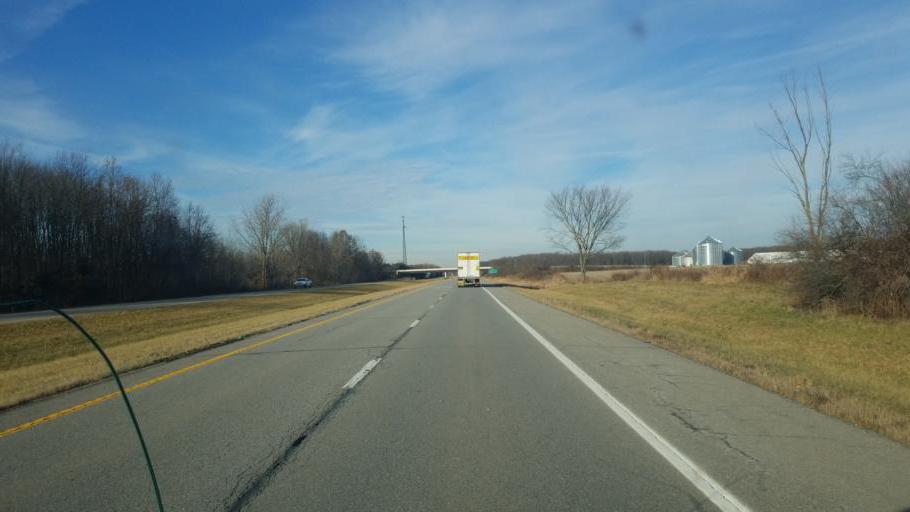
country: US
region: Ohio
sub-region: Trumbull County
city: Cortland
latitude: 41.4728
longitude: -80.7120
